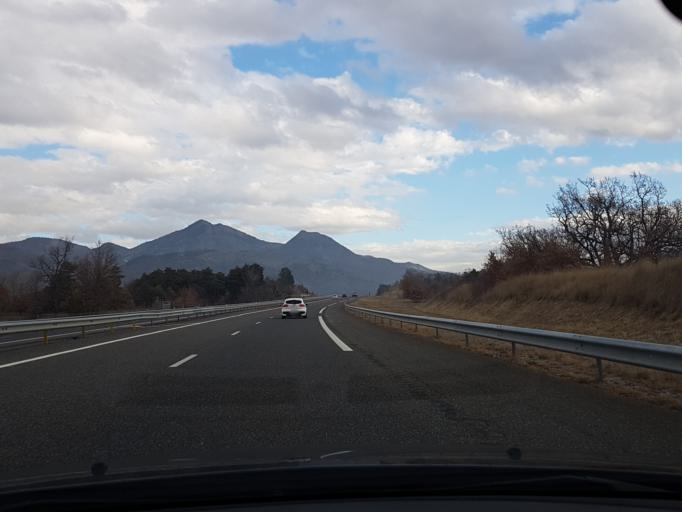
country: FR
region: Provence-Alpes-Cote d'Azur
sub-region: Departement des Hautes-Alpes
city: Tallard
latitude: 44.4071
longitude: 5.9581
